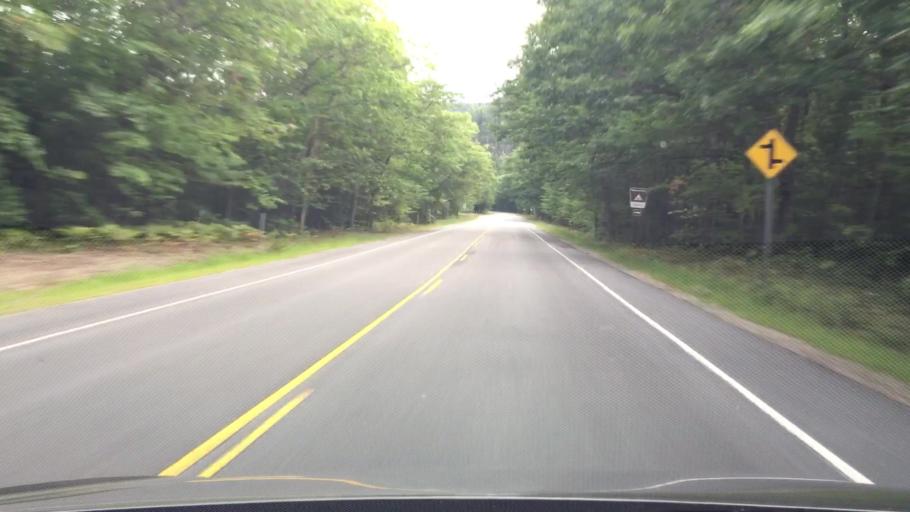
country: US
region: New Hampshire
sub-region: Carroll County
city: North Conway
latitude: 44.0084
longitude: -71.2435
